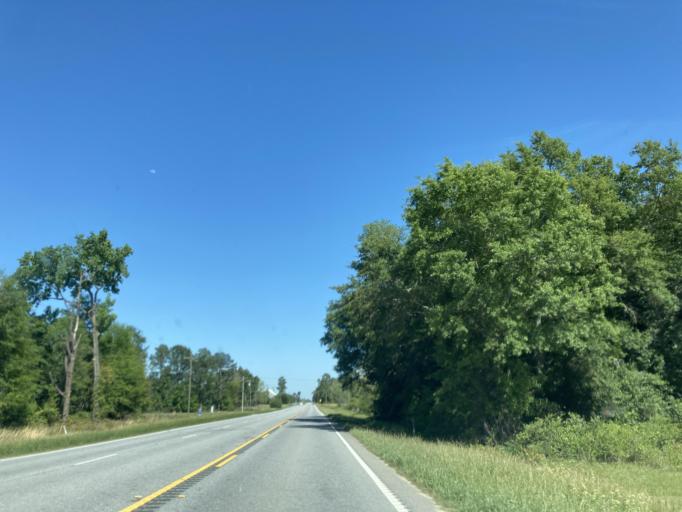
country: US
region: Georgia
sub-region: Miller County
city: Colquitt
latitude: 31.1856
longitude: -84.6106
